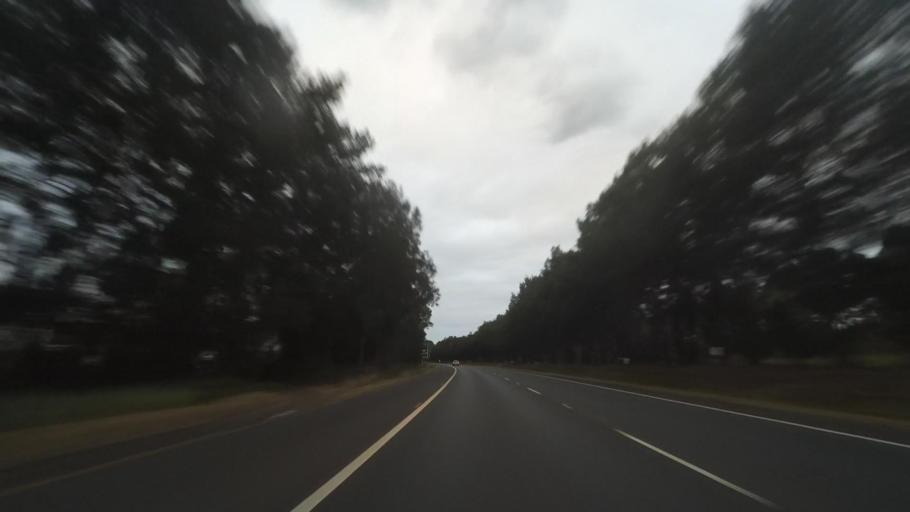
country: AU
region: New South Wales
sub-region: Wollongong
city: Berkeley
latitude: -34.4640
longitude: 150.8495
